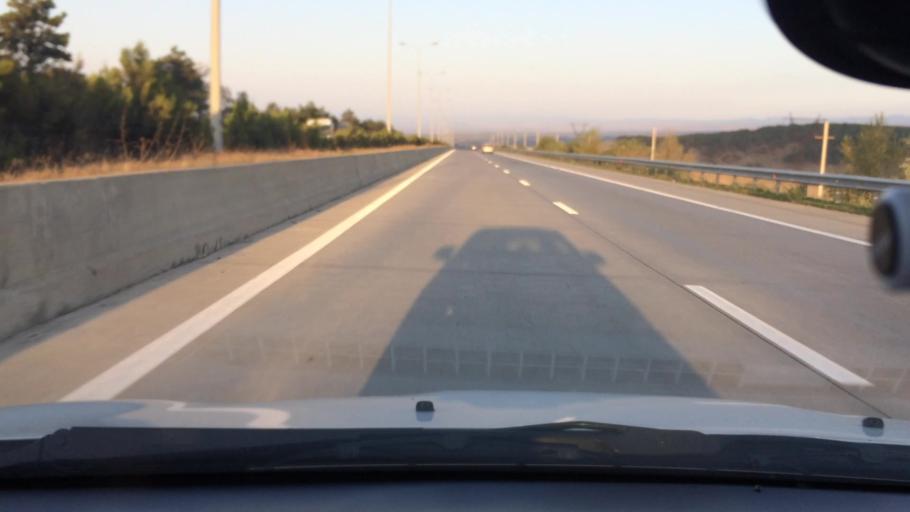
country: GE
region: Shida Kartli
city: Gori
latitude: 42.0192
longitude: 44.0144
